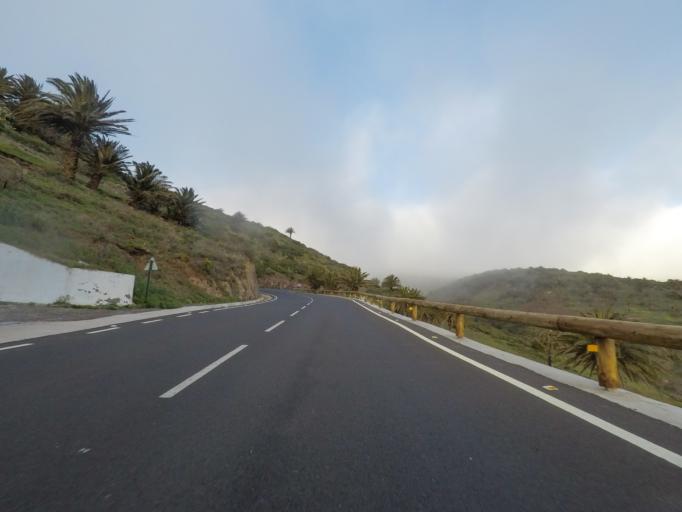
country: ES
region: Canary Islands
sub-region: Provincia de Santa Cruz de Tenerife
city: Vallehermosa
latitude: 28.1409
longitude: -17.3097
